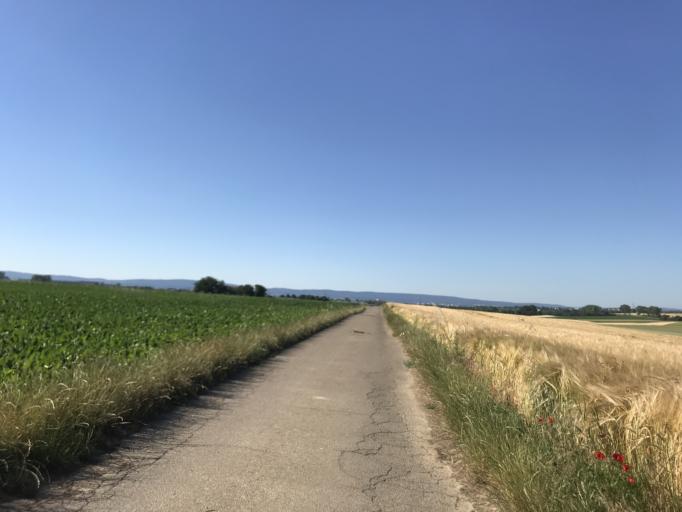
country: DE
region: Rheinland-Pfalz
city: Gau-Bischofsheim
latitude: 49.9338
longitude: 8.2749
